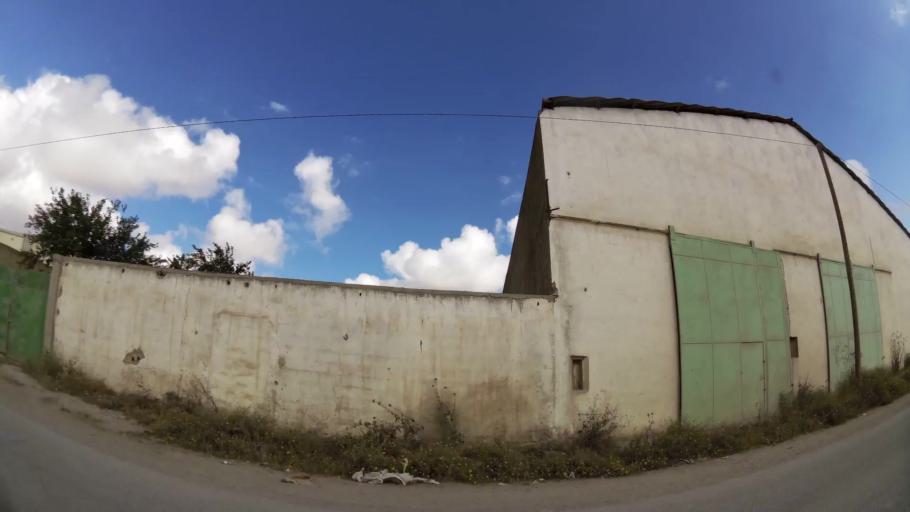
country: MA
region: Gharb-Chrarda-Beni Hssen
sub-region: Kenitra Province
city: Kenitra
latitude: 34.2714
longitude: -6.5658
